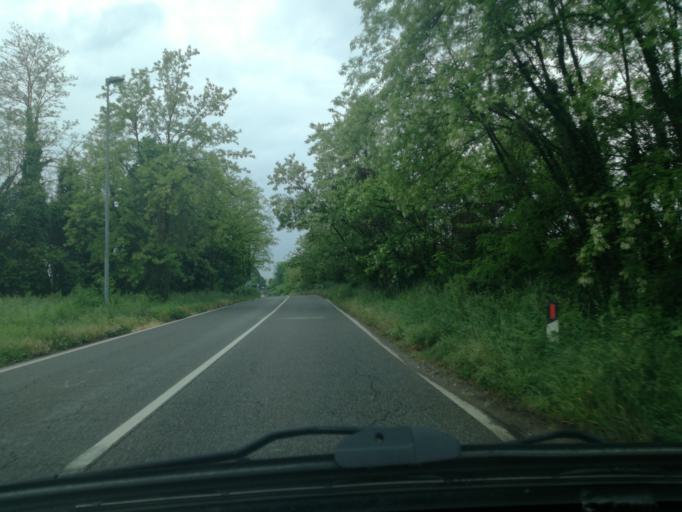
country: IT
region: Lombardy
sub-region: Provincia di Monza e Brianza
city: Triuggio
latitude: 45.6524
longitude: 9.2751
